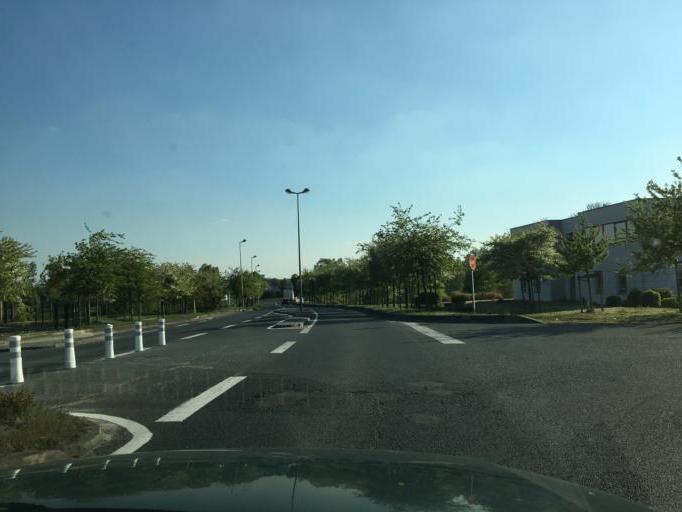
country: FR
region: Centre
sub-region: Departement du Loiret
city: Ormes
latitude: 47.9544
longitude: 1.8439
